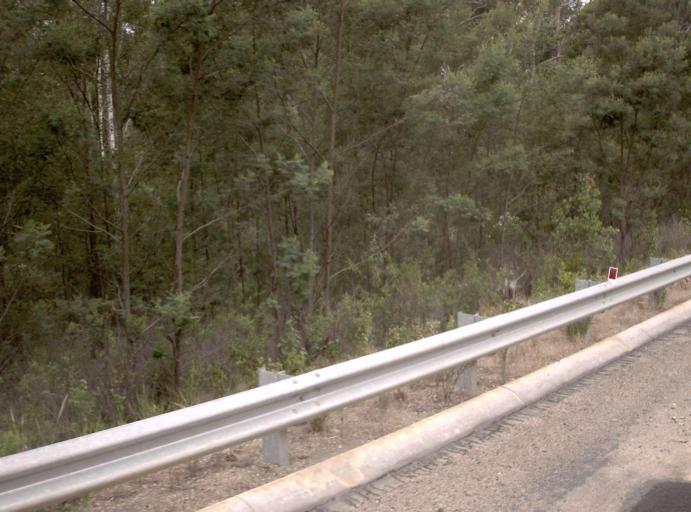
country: AU
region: Victoria
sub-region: East Gippsland
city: Lakes Entrance
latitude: -37.7217
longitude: 148.0829
